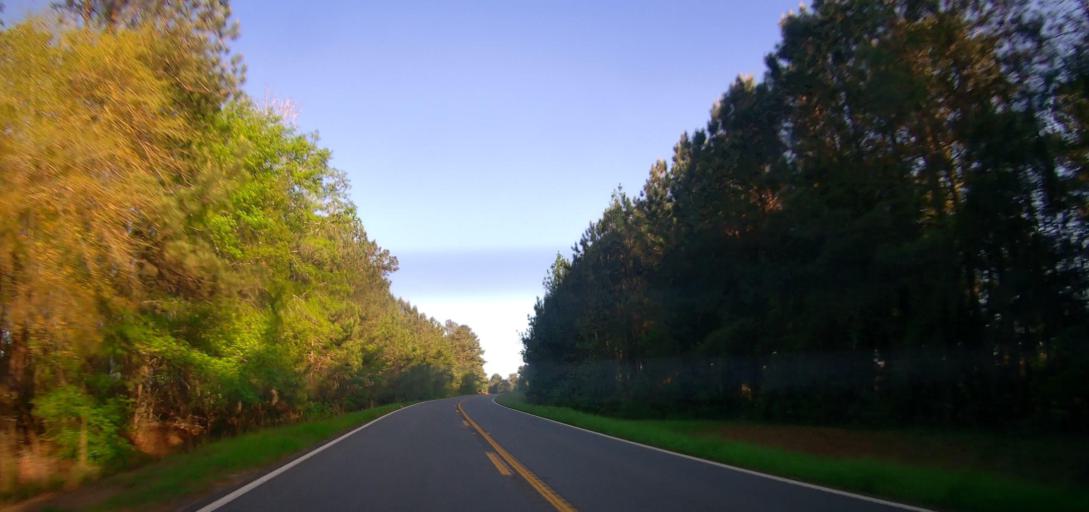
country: US
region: Georgia
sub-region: Marion County
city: Buena Vista
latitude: 32.3656
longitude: -84.4113
